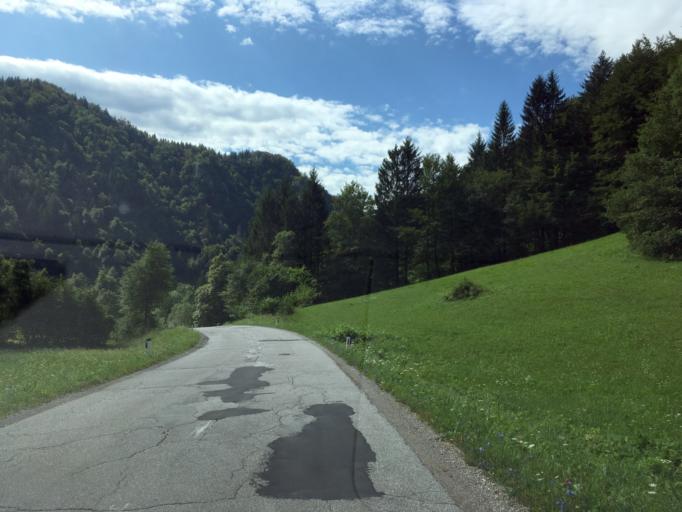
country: SI
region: Jesenice
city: Slovenski Javornik
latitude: 46.4083
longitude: 14.0773
